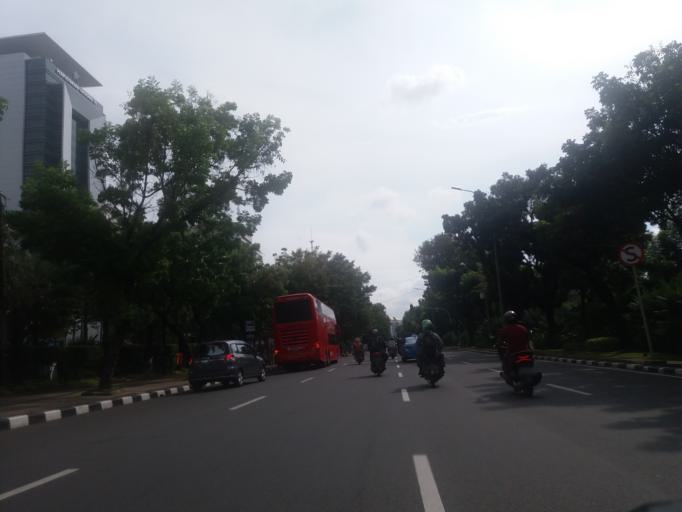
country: ID
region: Jakarta Raya
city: Jakarta
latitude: -6.1805
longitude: 106.8288
